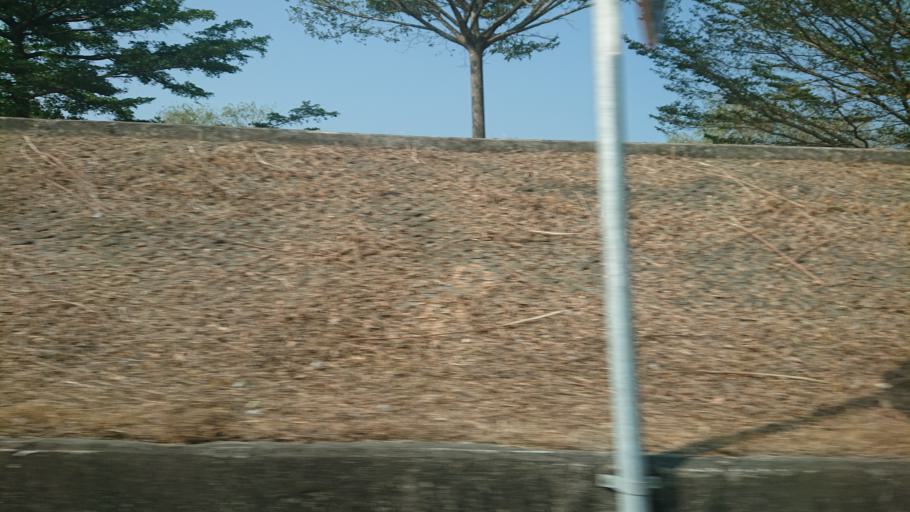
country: TW
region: Taiwan
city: Lugu
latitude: 23.7564
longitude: 120.6590
